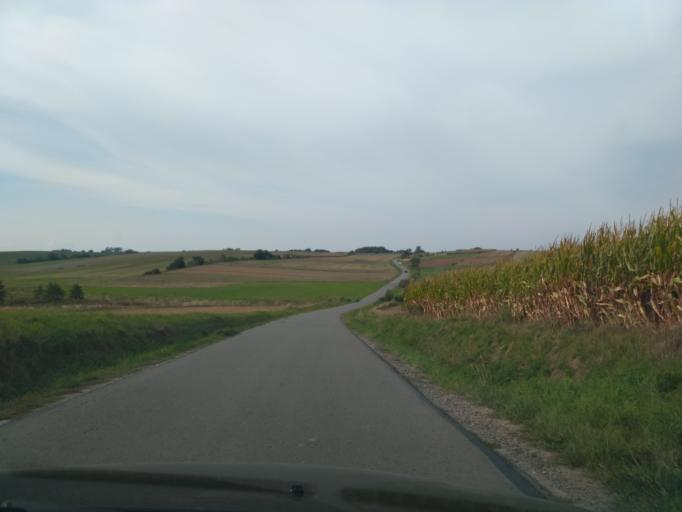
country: PL
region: Subcarpathian Voivodeship
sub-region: Powiat rzeszowski
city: Zglobien
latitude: 50.0171
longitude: 21.8490
